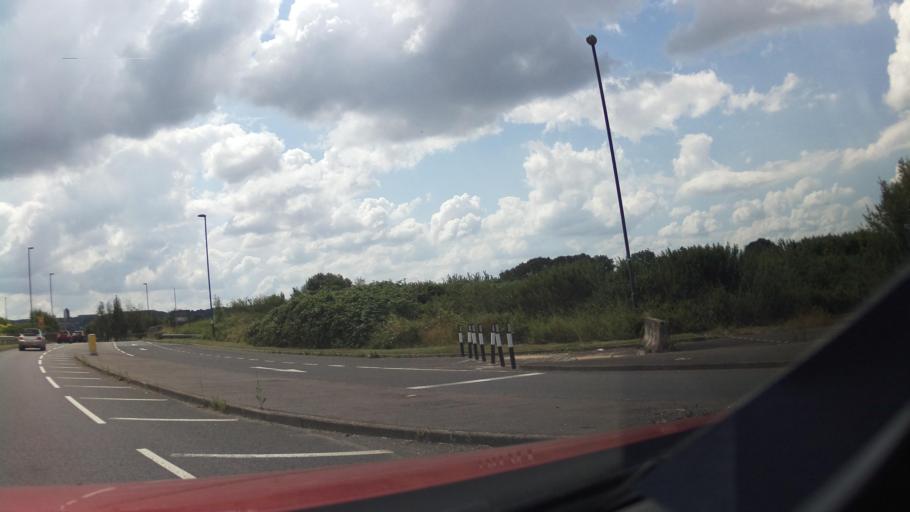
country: GB
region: England
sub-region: Borough of Swindon
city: Wroughton
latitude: 51.5423
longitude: -1.8014
